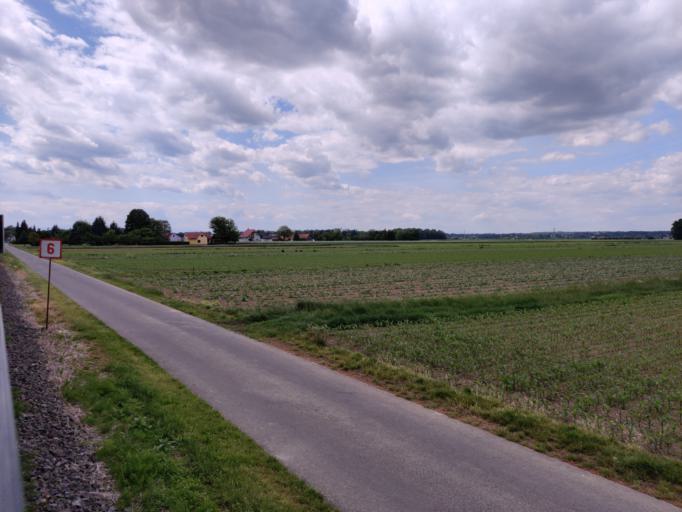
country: AT
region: Styria
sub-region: Politischer Bezirk Suedoststeiermark
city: Weinburg am Sassbach
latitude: 46.7146
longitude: 15.7276
